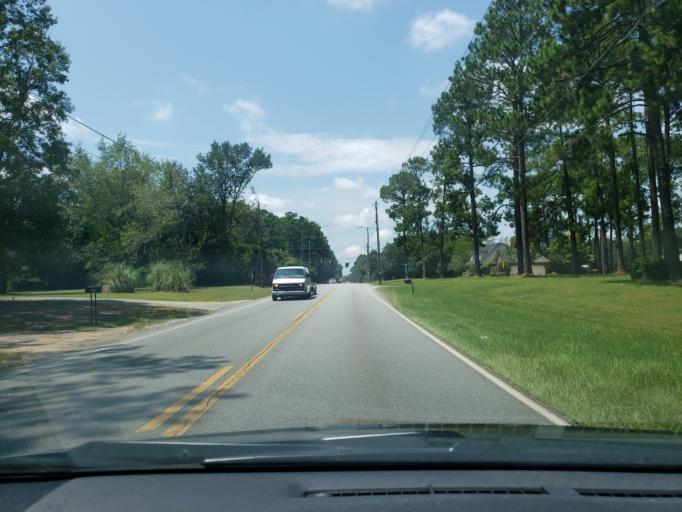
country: US
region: Georgia
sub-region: Dougherty County
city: Albany
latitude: 31.6135
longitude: -84.2341
